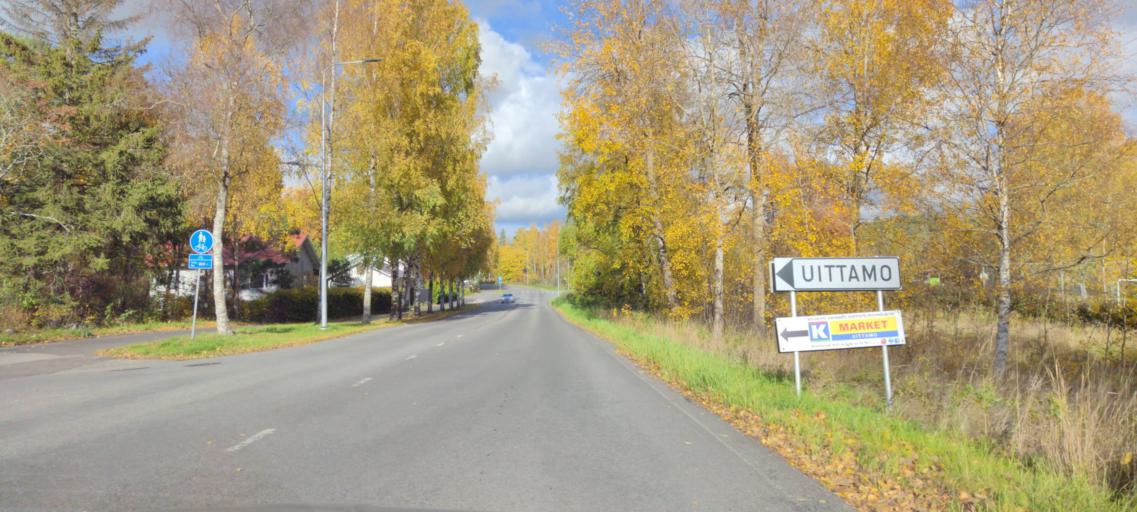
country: FI
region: Varsinais-Suomi
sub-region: Turku
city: Turku
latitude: 60.4215
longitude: 22.2702
